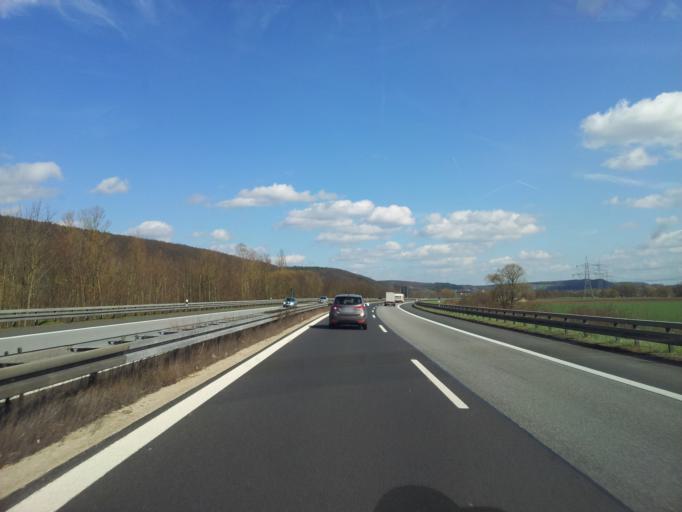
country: DE
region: Bavaria
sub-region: Regierungsbezirk Unterfranken
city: Ebelsbach
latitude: 49.9779
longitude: 10.6805
